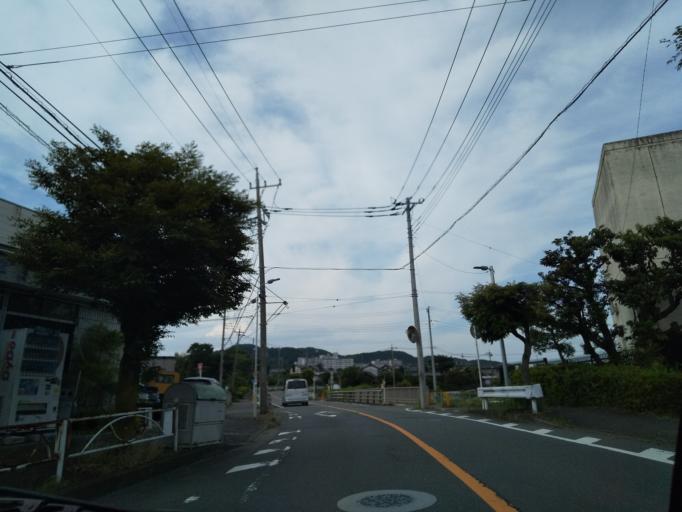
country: JP
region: Kanagawa
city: Atsugi
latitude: 35.4841
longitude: 139.3228
